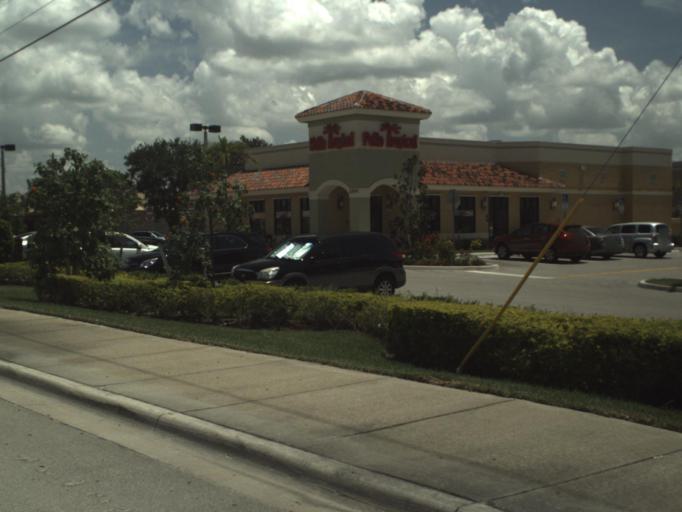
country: US
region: Florida
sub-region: Martin County
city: Stuart
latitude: 27.1789
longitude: -80.2379
